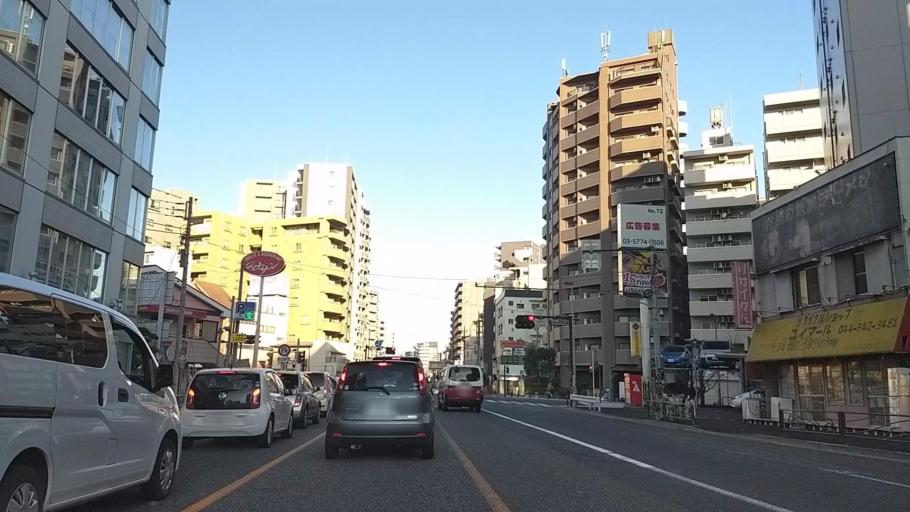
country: JP
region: Kanagawa
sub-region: Kawasaki-shi
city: Kawasaki
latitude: 35.5310
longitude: 139.6909
